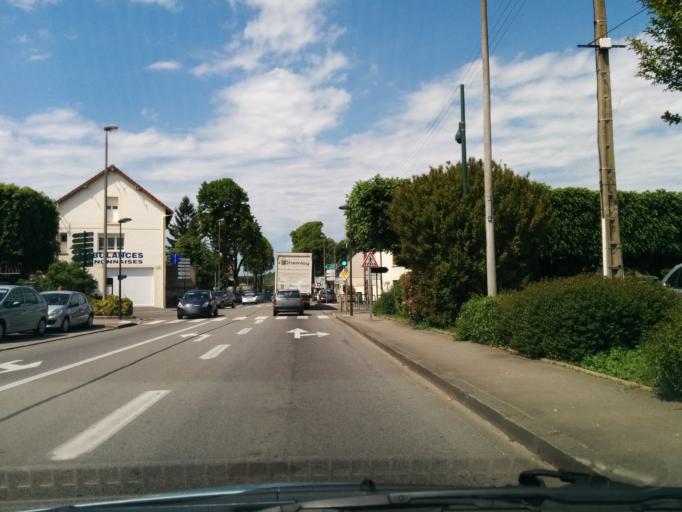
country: FR
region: Haute-Normandie
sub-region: Departement de l'Eure
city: Vernon
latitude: 49.0921
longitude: 1.4889
